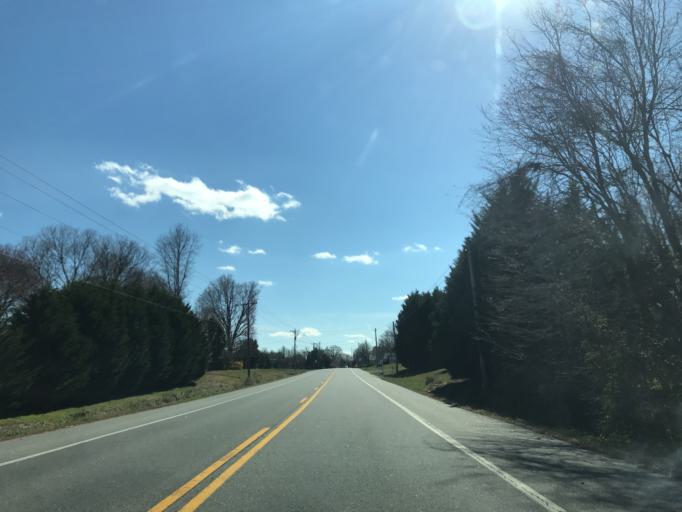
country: US
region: Maryland
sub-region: Kent County
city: Rock Hall
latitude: 39.1590
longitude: -76.2059
